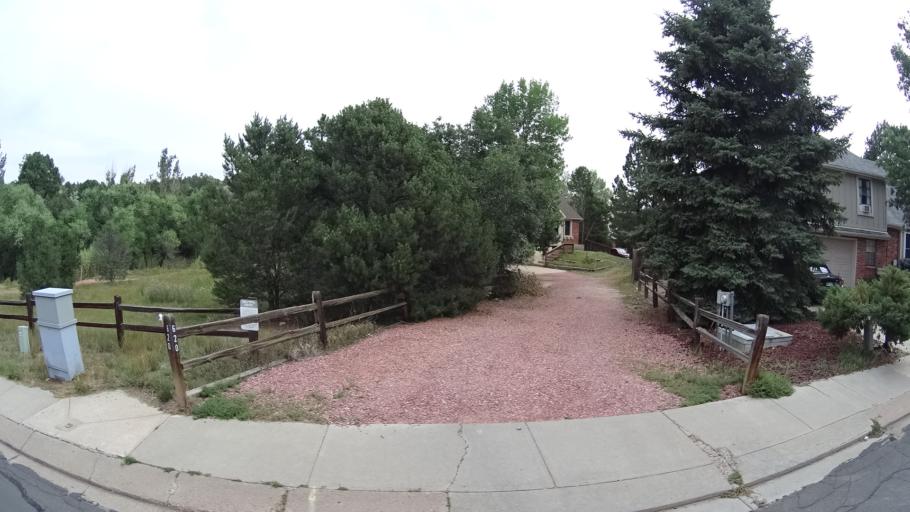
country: US
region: Colorado
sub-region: El Paso County
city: Air Force Academy
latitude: 38.9292
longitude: -104.8387
